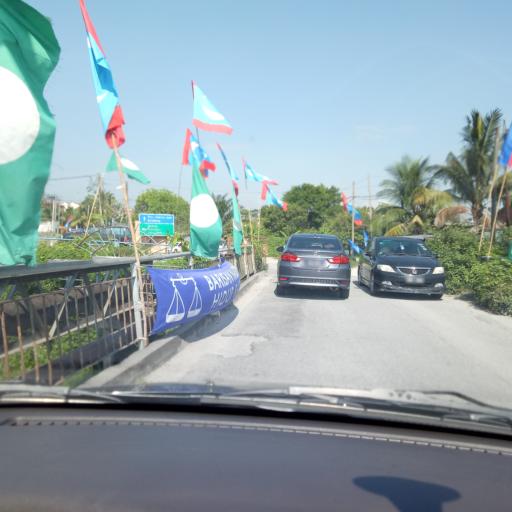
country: MY
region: Selangor
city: Kampong Baharu Balakong
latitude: 3.0143
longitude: 101.7703
